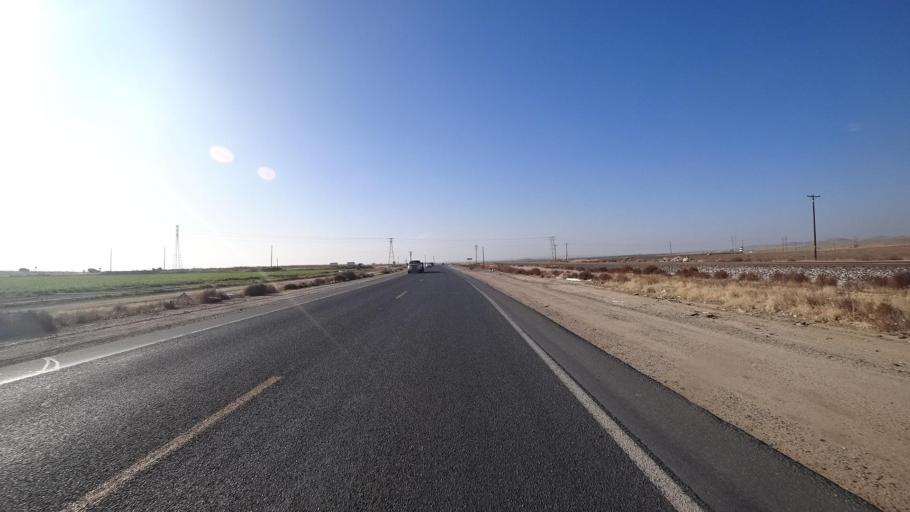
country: US
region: California
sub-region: Kern County
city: Arvin
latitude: 35.3321
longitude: -118.8053
